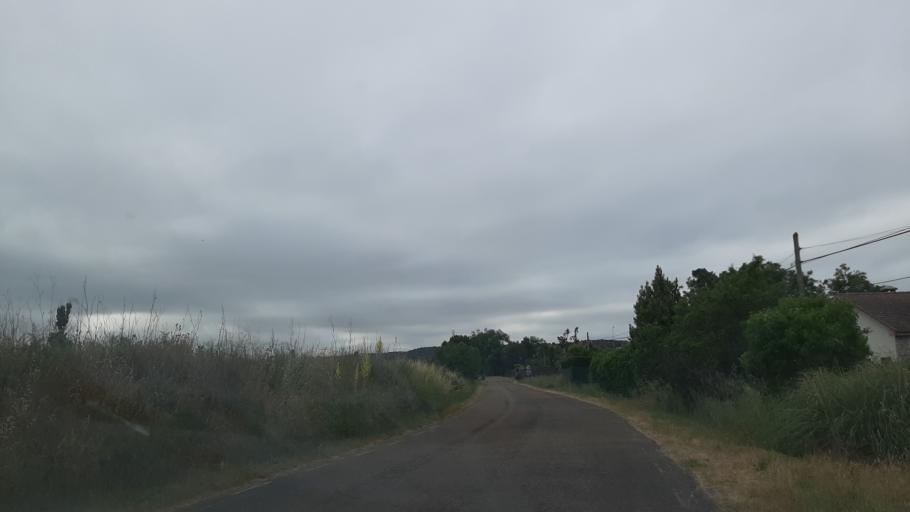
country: ES
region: Castille and Leon
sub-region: Provincia de Salamanca
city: Ciudad Rodrigo
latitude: 40.5671
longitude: -6.4882
